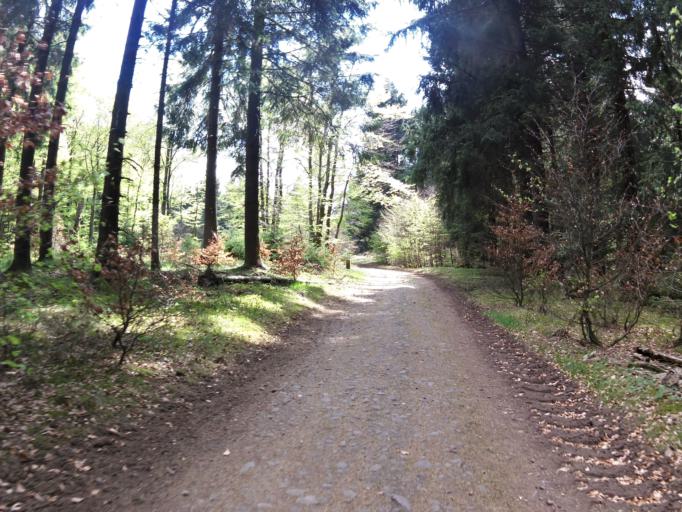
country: DE
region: Thuringia
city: Friedrichroda
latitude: 50.8231
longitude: 10.5402
